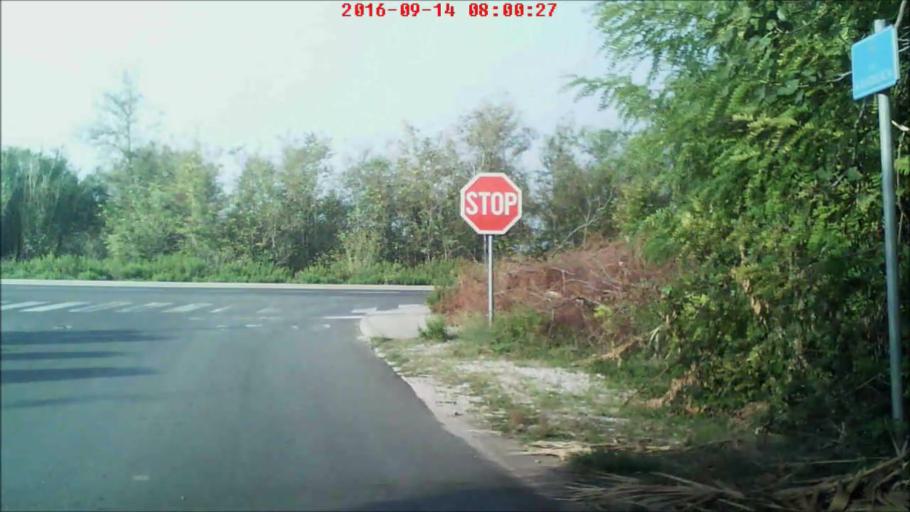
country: HR
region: Zadarska
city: Nin
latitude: 44.2565
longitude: 15.1559
